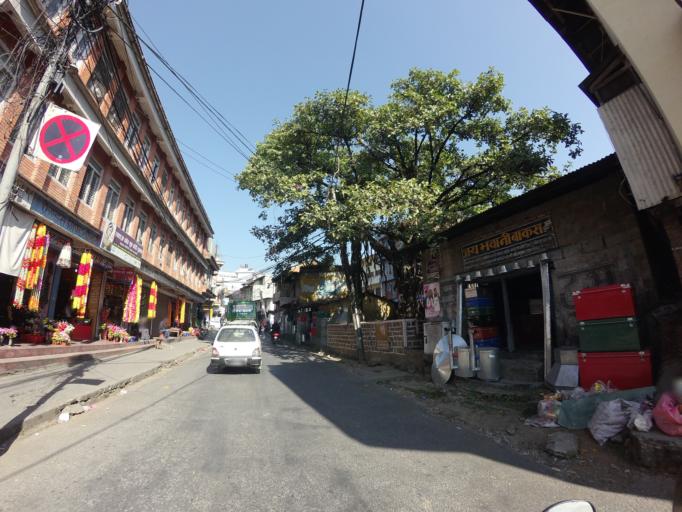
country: NP
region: Western Region
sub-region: Gandaki Zone
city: Pokhara
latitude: 28.2259
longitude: 83.9909
